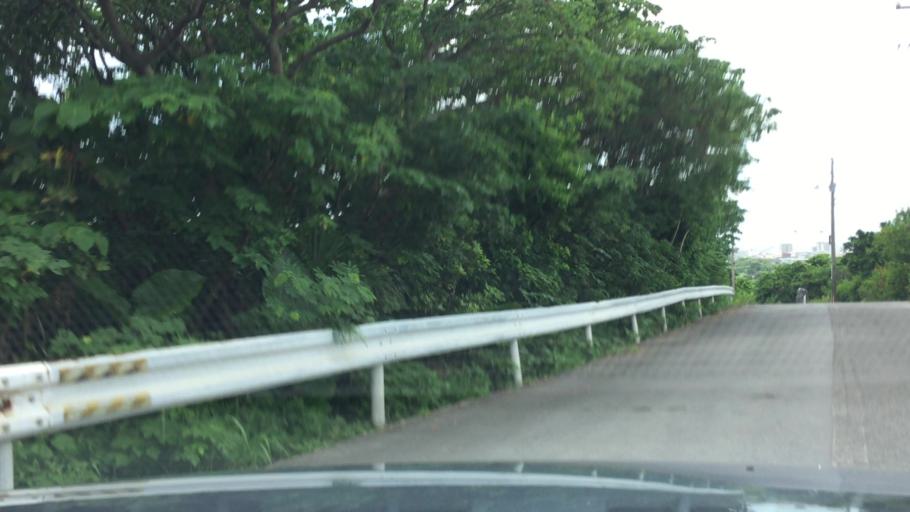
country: JP
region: Okinawa
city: Ishigaki
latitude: 24.3609
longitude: 124.1547
